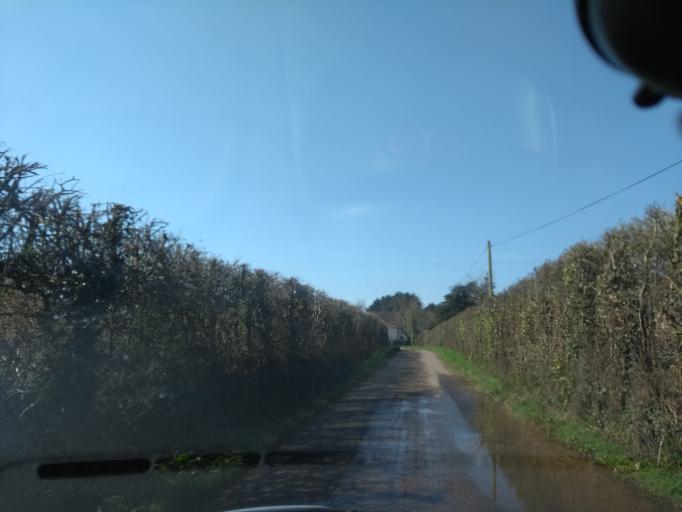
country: GB
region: England
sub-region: Somerset
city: Taunton
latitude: 51.0465
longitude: -3.1158
